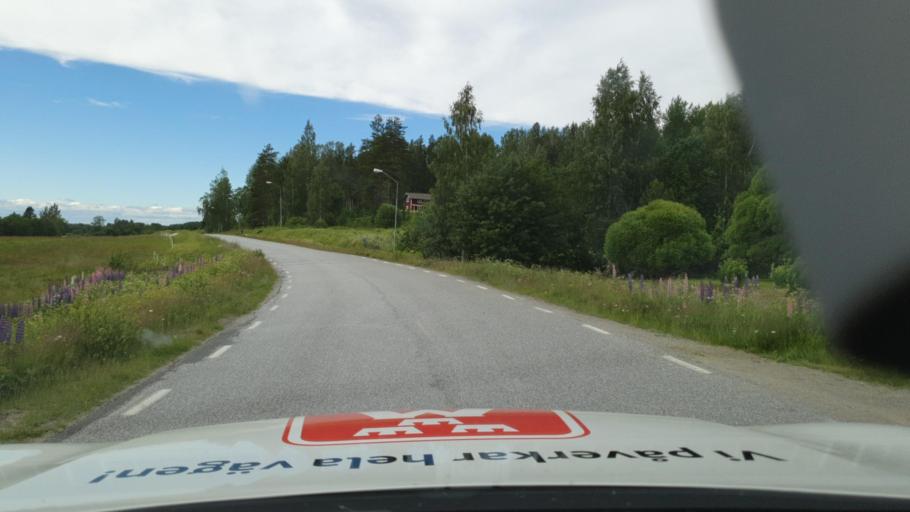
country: SE
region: Vaesterbotten
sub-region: Skelleftea Kommun
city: Burea
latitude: 64.4901
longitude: 21.0327
